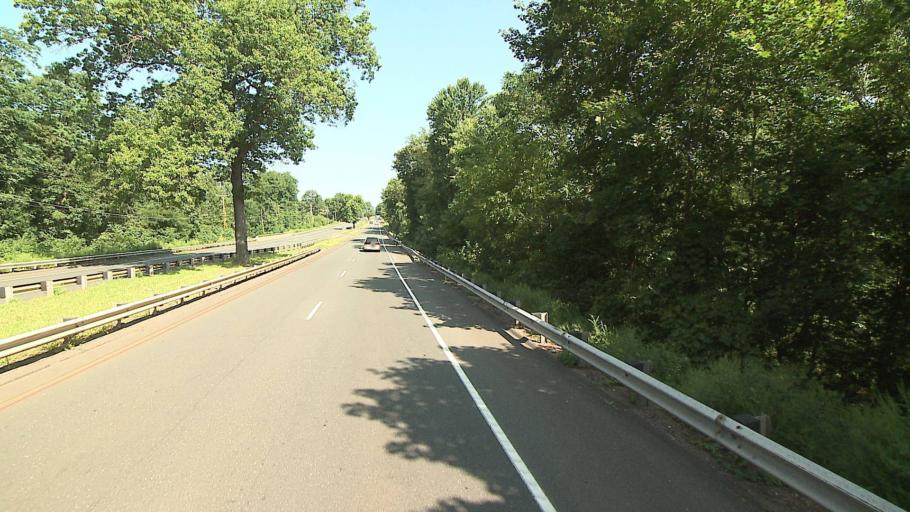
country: US
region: Connecticut
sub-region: Hartford County
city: Windsor
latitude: 41.8610
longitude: -72.6031
